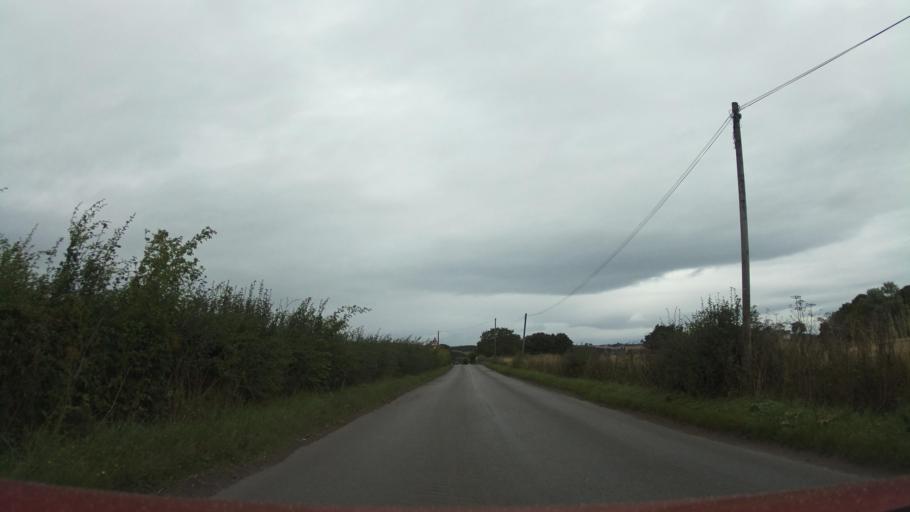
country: GB
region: Scotland
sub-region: Perth and Kinross
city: Milnathort
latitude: 56.2330
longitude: -3.3636
